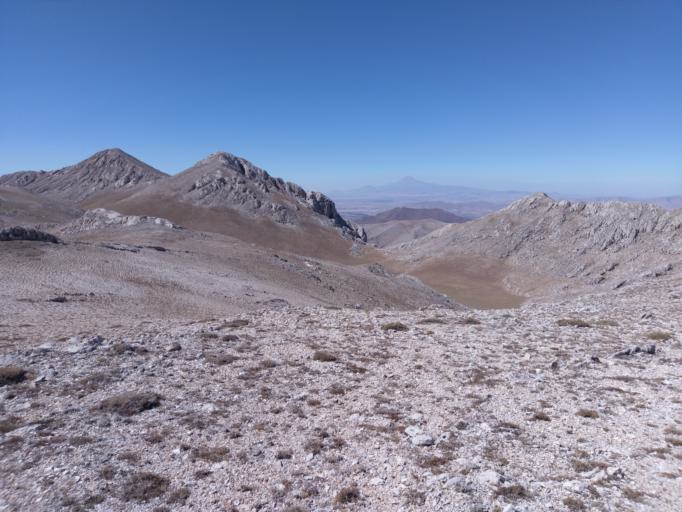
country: TR
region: Adana
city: Tufanbeyli
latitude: 38.3546
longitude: 36.1563
